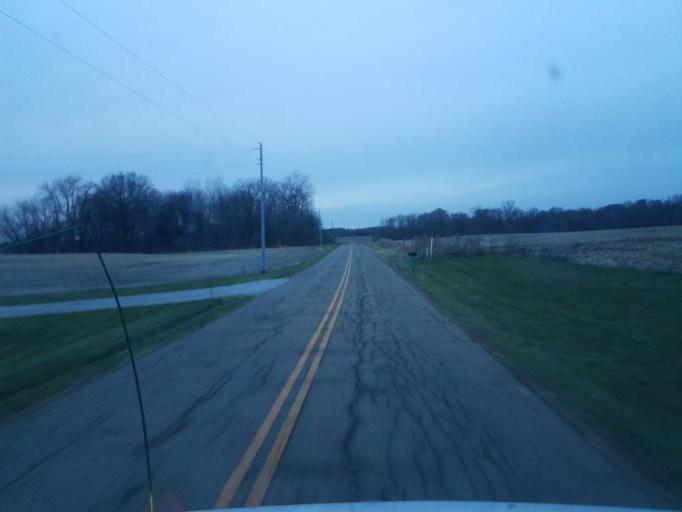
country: US
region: Ohio
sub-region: Licking County
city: Utica
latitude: 40.2993
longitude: -82.4396
